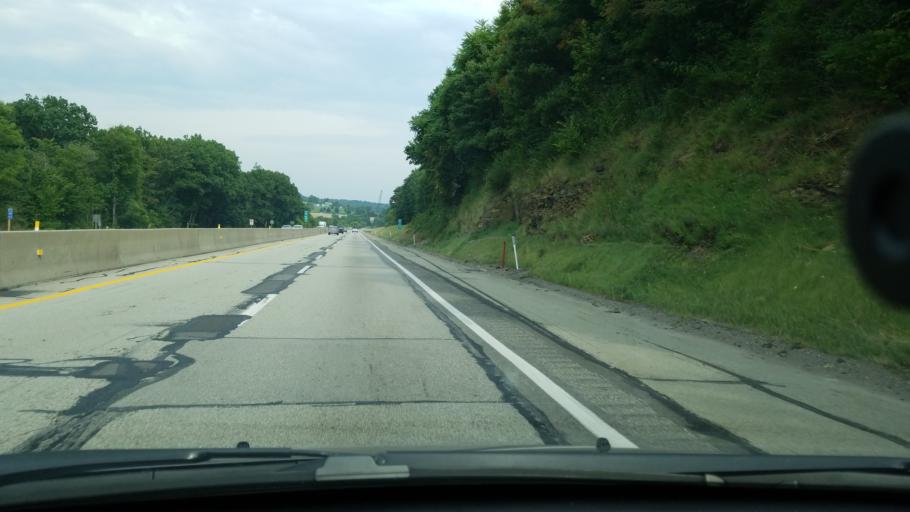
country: US
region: Pennsylvania
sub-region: Beaver County
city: Freedom
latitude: 40.7564
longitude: -80.2234
